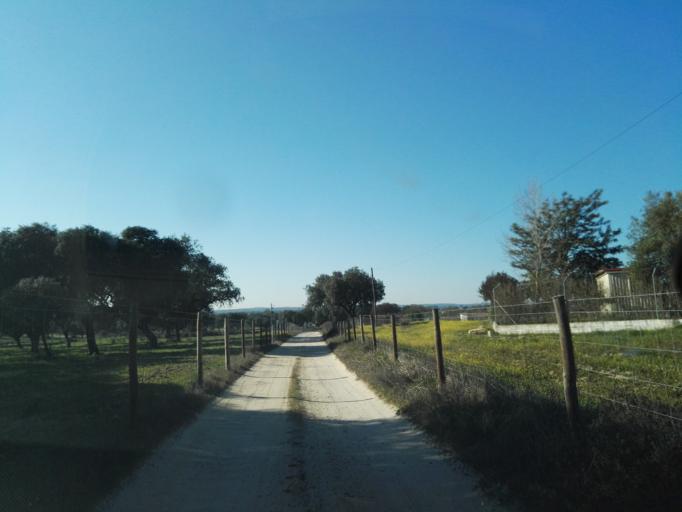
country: PT
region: Evora
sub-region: Evora
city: Evora
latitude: 38.5444
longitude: -7.9486
